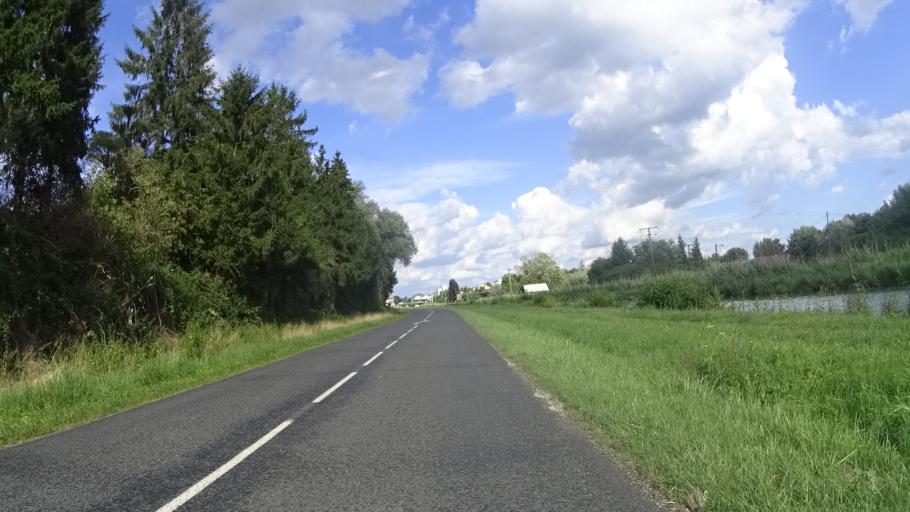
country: FR
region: Champagne-Ardenne
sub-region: Departement de la Marne
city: Sermaize-les-Bains
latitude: 48.7892
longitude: 4.8996
